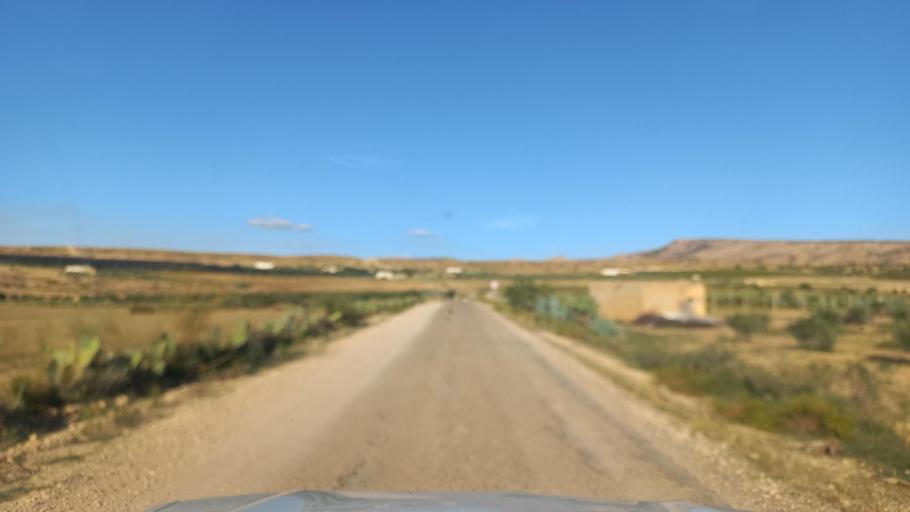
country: TN
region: Al Qasrayn
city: Sbiba
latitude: 35.3416
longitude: 9.1220
